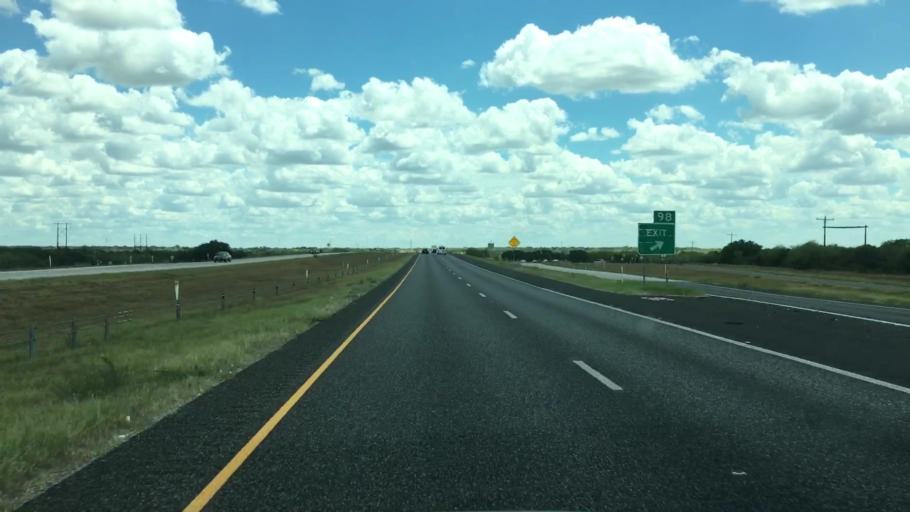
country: US
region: Texas
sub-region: Atascosa County
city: Pleasanton
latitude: 28.8472
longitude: -98.3794
